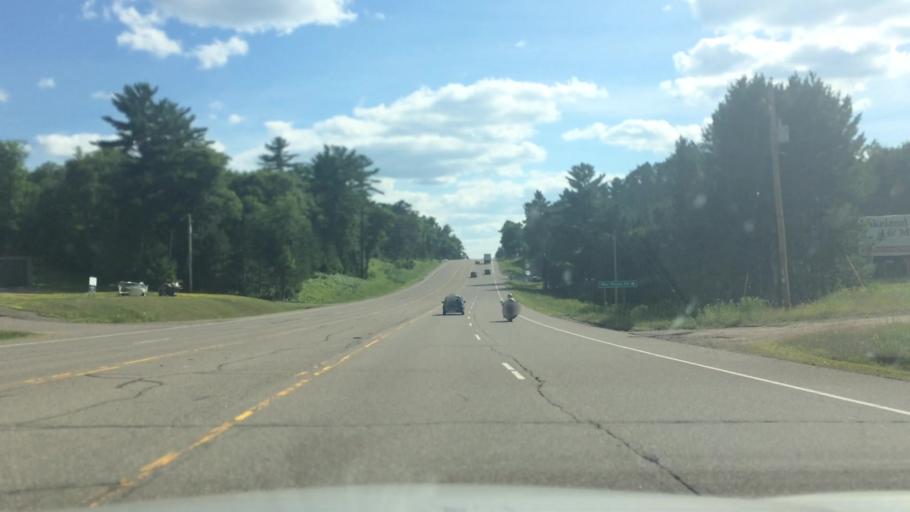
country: US
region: Wisconsin
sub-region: Vilas County
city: Lac du Flambeau
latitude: 45.8380
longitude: -89.7091
